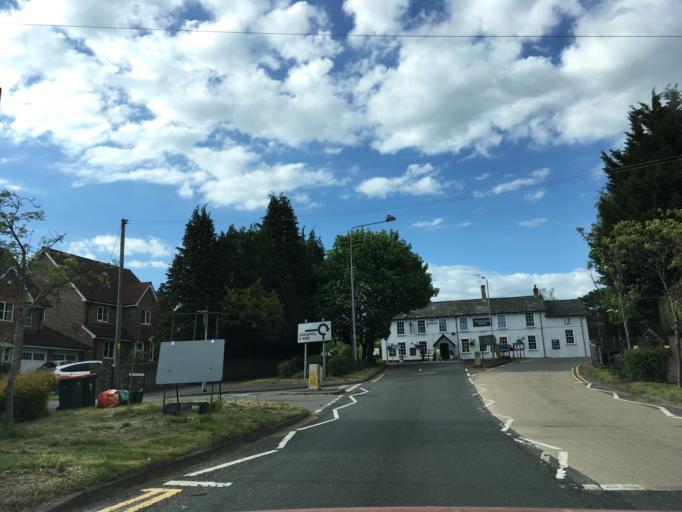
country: GB
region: Wales
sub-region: Newport
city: Newport
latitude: 51.5768
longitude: -3.0448
